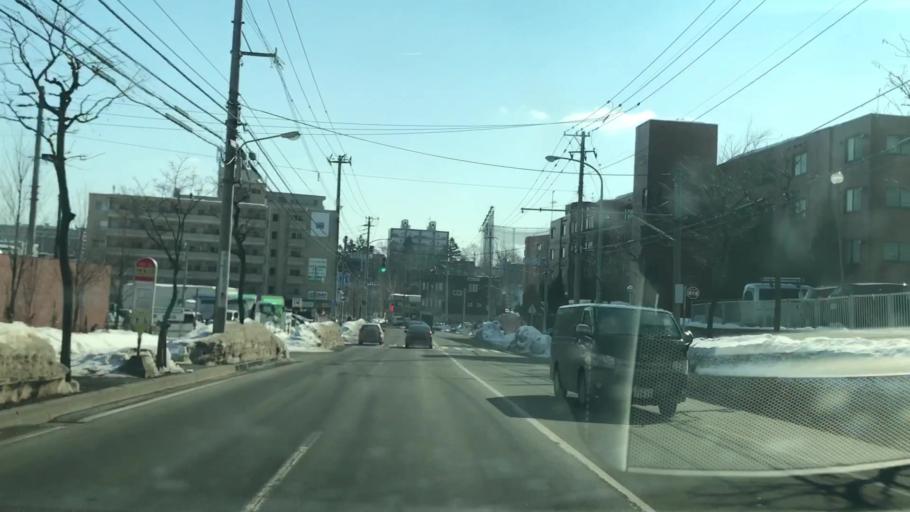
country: JP
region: Hokkaido
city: Sapporo
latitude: 43.0244
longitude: 141.3825
